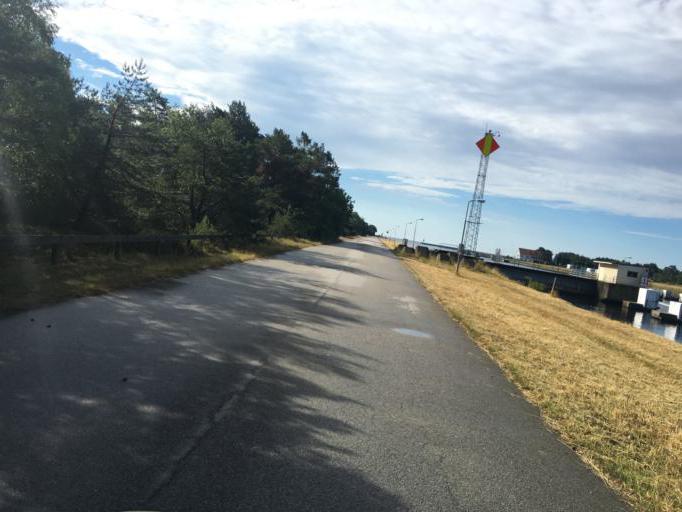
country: SE
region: Skane
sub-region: Vellinge Kommun
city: Hollviken
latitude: 55.4023
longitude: 12.9422
